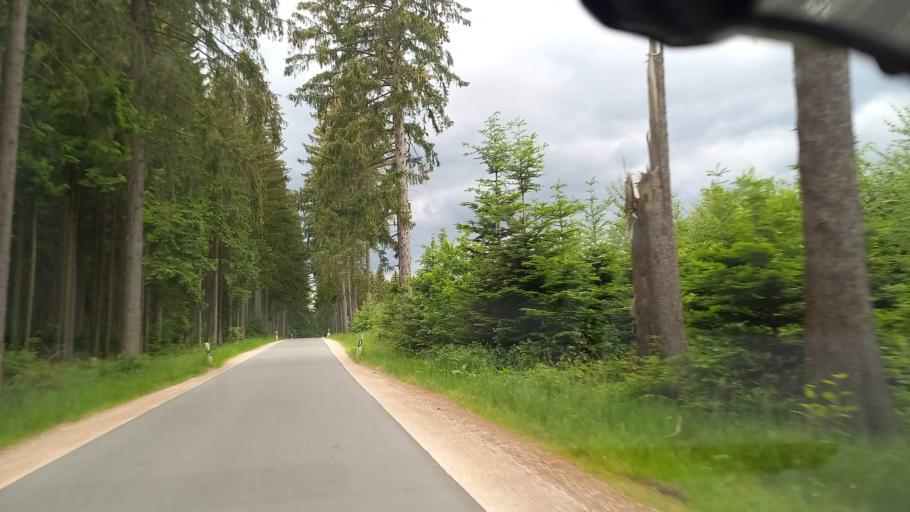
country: DE
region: Saxony
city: Stutzengrun
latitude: 50.5443
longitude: 12.4798
